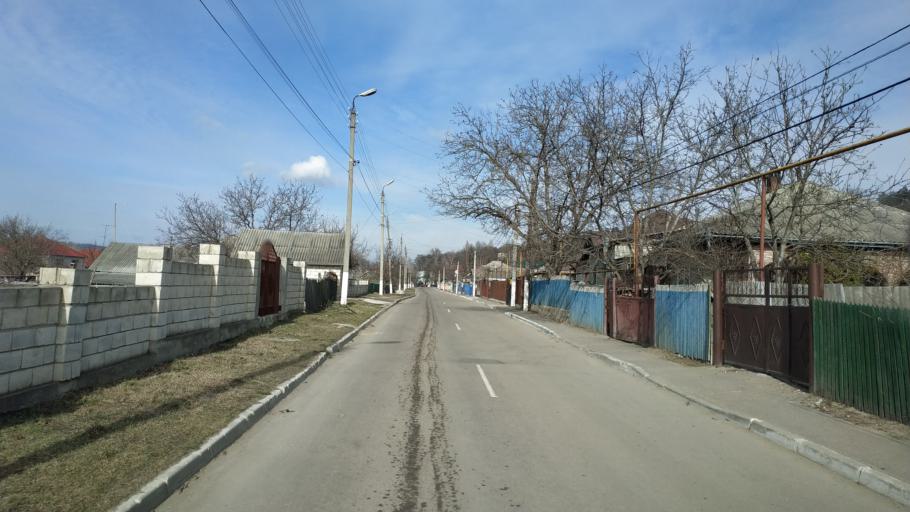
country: MD
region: Hincesti
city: Hincesti
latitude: 46.8315
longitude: 28.6036
